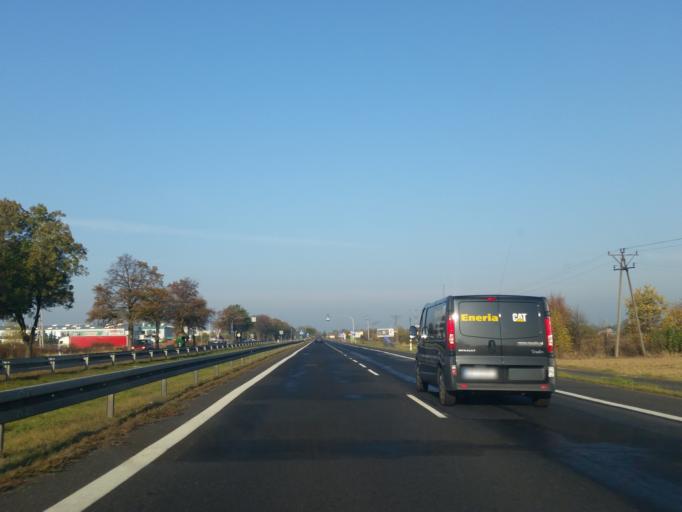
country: PL
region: Masovian Voivodeship
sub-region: Powiat nowodworski
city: Nowy Dwor Mazowiecki
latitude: 52.3832
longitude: 20.7556
